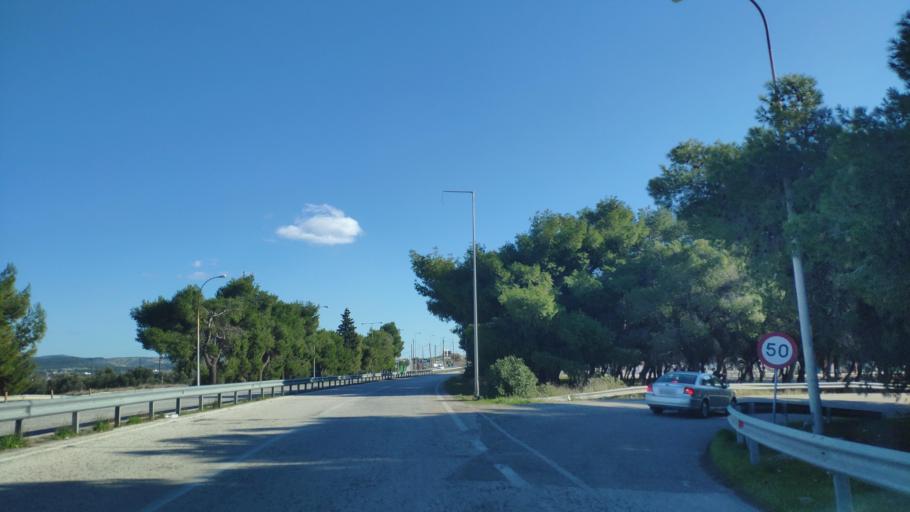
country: GR
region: Peloponnese
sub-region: Nomos Korinthias
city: Korinthos
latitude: 37.9370
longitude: 22.9553
